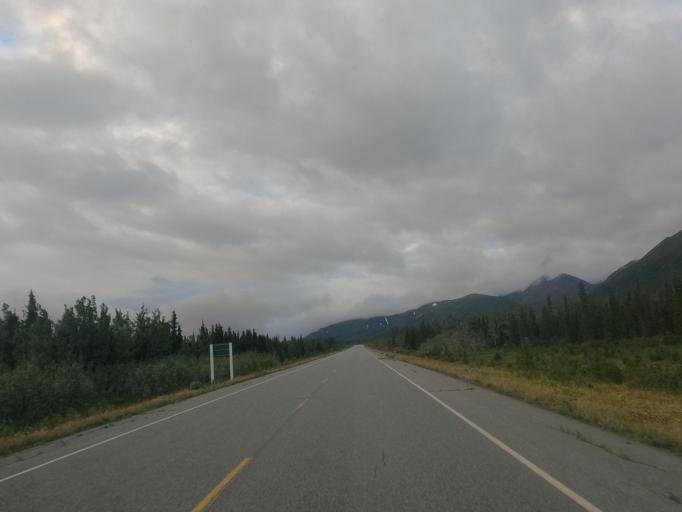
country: CA
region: Yukon
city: Haines Junction
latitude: 60.3209
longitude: -137.0441
